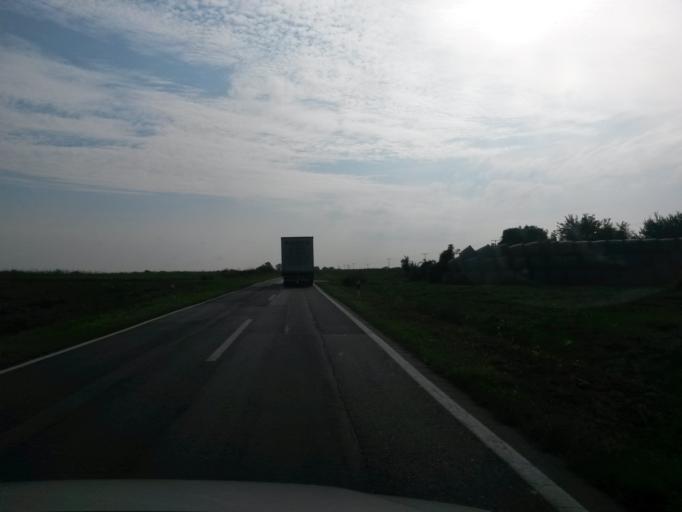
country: HR
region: Vukovarsko-Srijemska
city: Lovas
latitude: 45.2528
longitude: 19.2007
